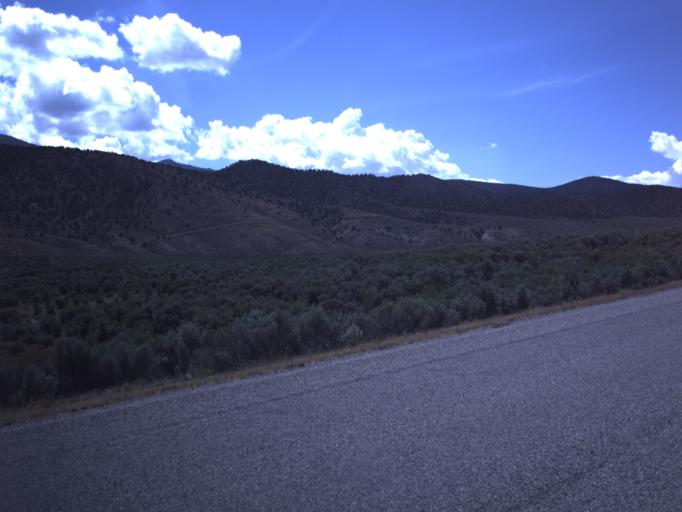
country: US
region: Utah
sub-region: Piute County
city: Junction
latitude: 38.0468
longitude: -112.3538
